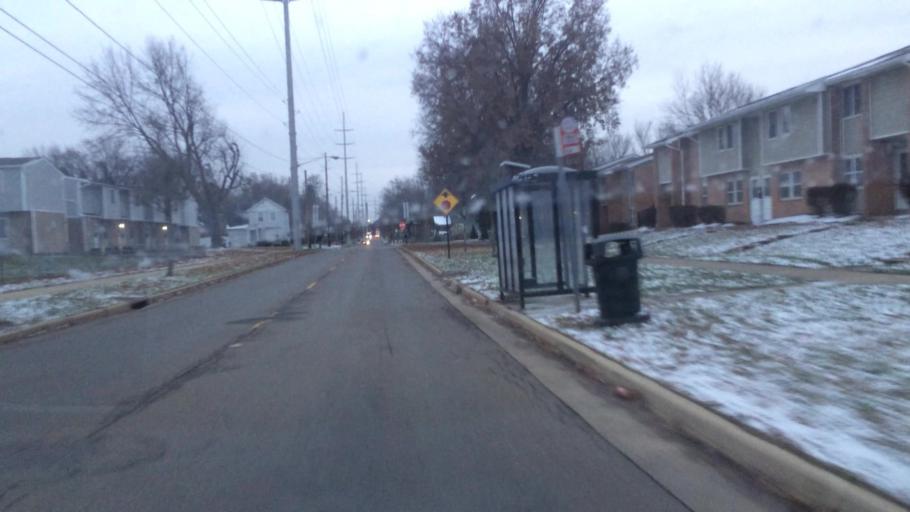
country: US
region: Ohio
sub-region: Summit County
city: Akron
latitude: 41.0553
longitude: -81.5414
